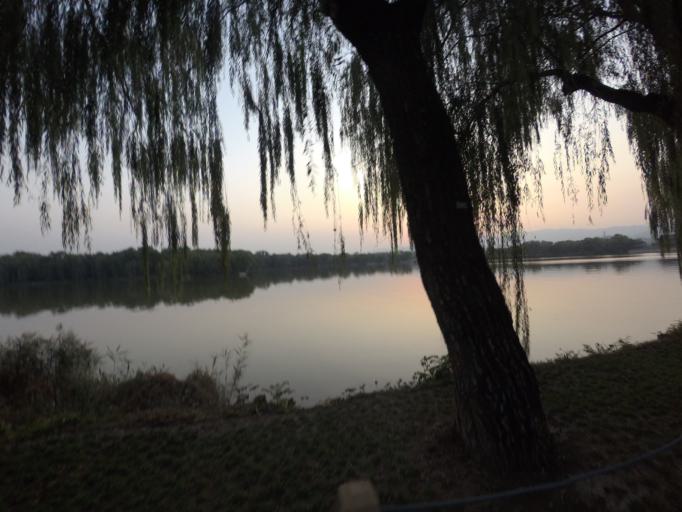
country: CN
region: Beijing
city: Haidian
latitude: 39.9831
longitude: 116.2721
